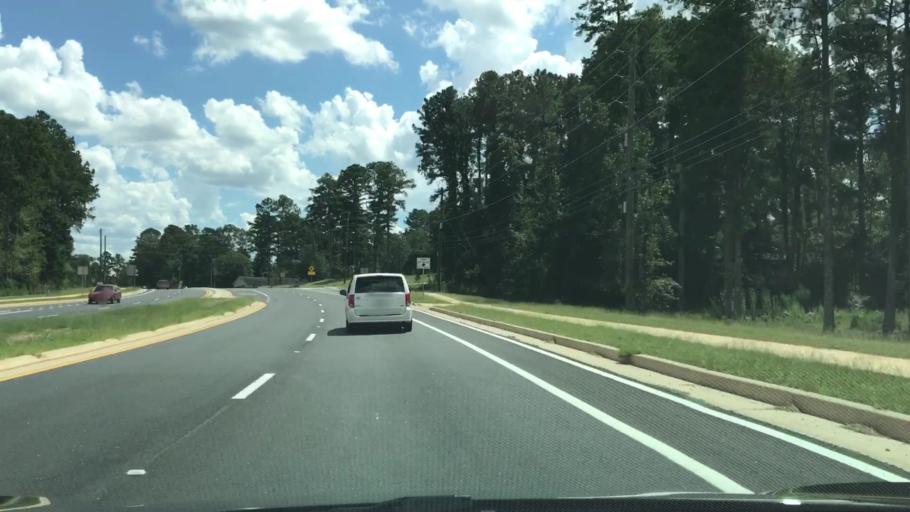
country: US
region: Georgia
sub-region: Oconee County
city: Watkinsville
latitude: 33.8814
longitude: -83.4546
